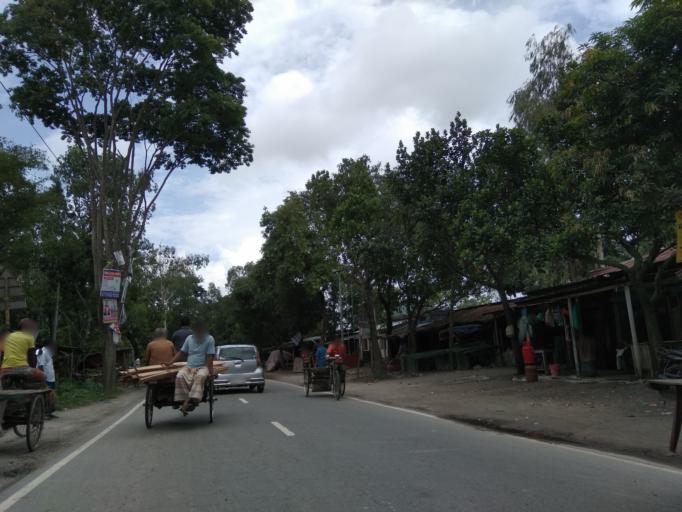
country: BD
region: Rajshahi
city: Saidpur
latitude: 25.7709
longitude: 88.8021
